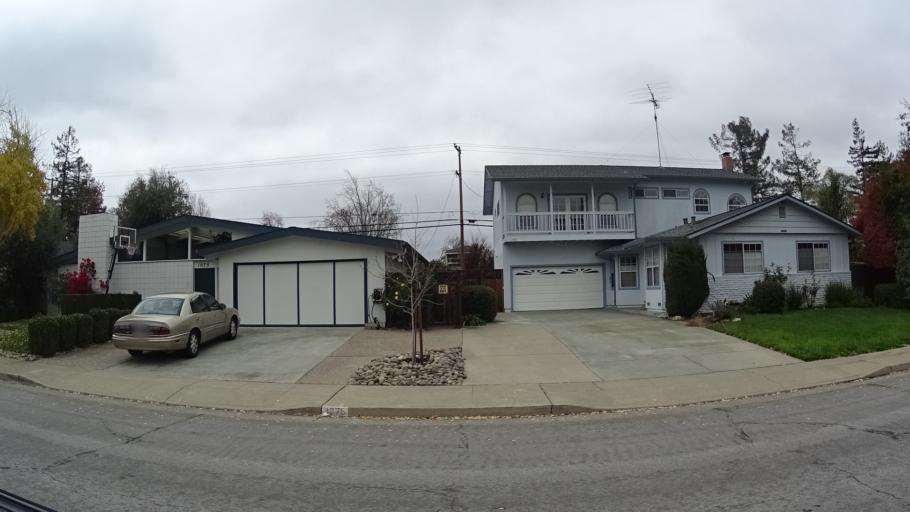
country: US
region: California
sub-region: Santa Clara County
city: Sunnyvale
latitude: 37.3559
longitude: -122.0227
